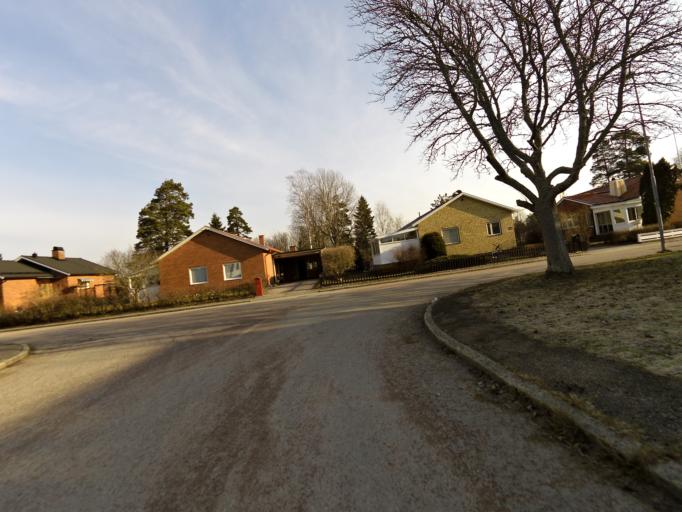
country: SE
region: Gaevleborg
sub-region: Gavle Kommun
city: Gavle
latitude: 60.6576
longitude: 17.1282
